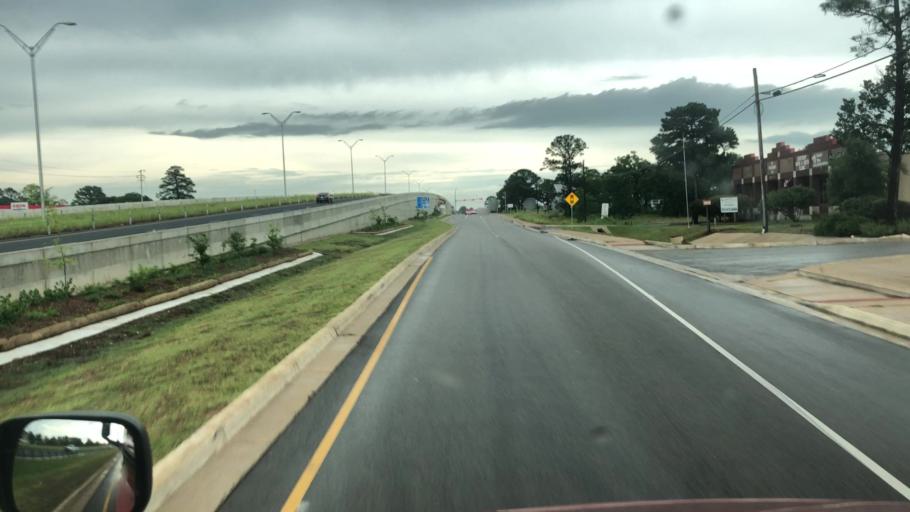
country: US
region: Texas
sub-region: Bastrop County
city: Bastrop
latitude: 30.1030
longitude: -97.2877
